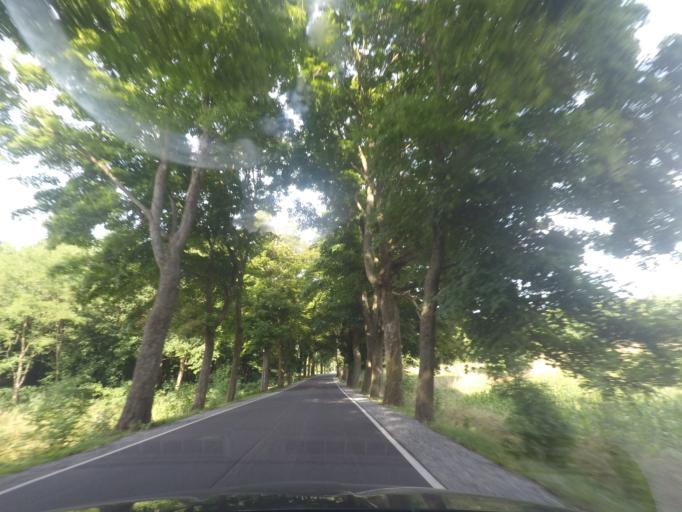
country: PL
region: Pomeranian Voivodeship
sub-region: Powiat leborski
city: Leba
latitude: 54.6367
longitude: 17.5242
